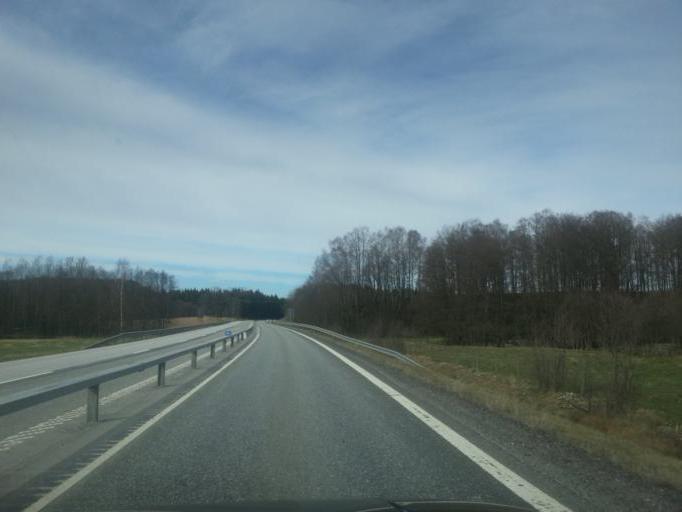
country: SE
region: Joenkoeping
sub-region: Jonkopings Kommun
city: Bankeryd
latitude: 57.8451
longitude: 14.1067
